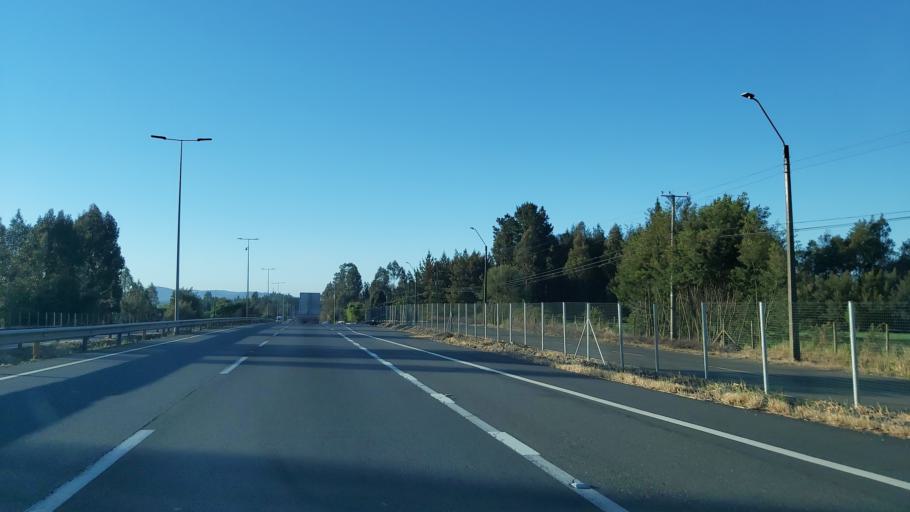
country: CL
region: Araucania
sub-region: Provincia de Malleco
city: Collipulli
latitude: -38.0845
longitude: -72.3650
